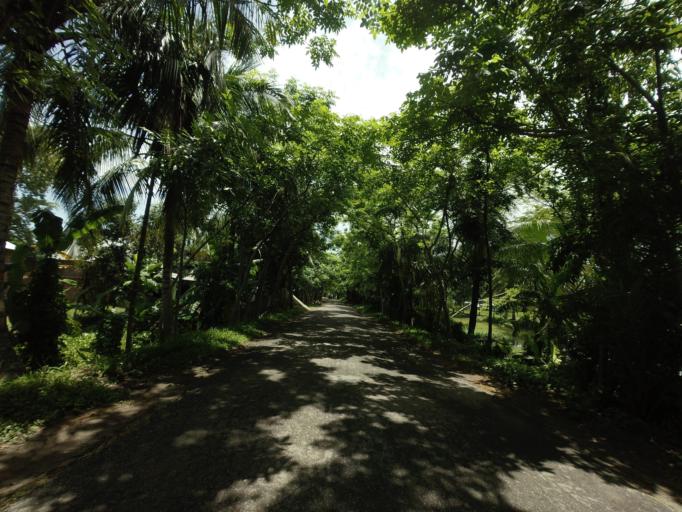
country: BD
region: Khulna
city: Kalia
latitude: 23.0401
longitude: 89.6404
